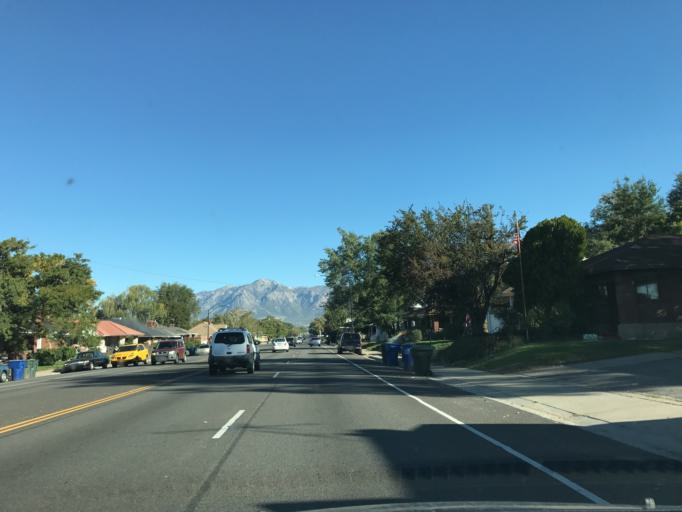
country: US
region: Utah
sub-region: Weber County
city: Ogden
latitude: 41.2186
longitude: -111.9482
